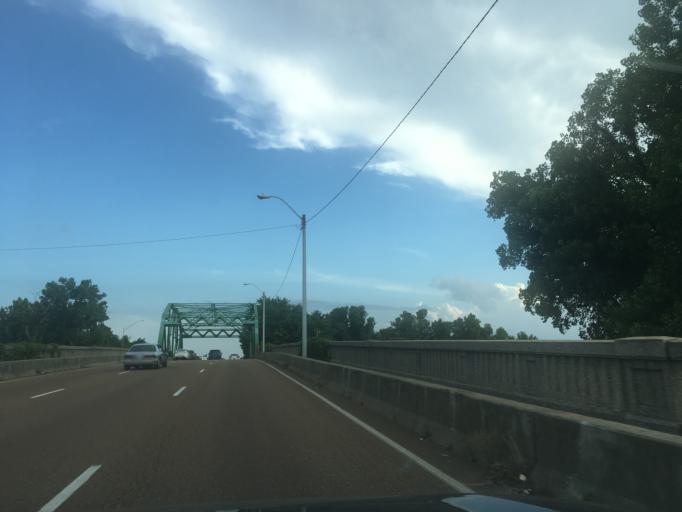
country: US
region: Tennessee
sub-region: Shelby County
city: New South Memphis
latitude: 35.0758
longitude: -90.0579
